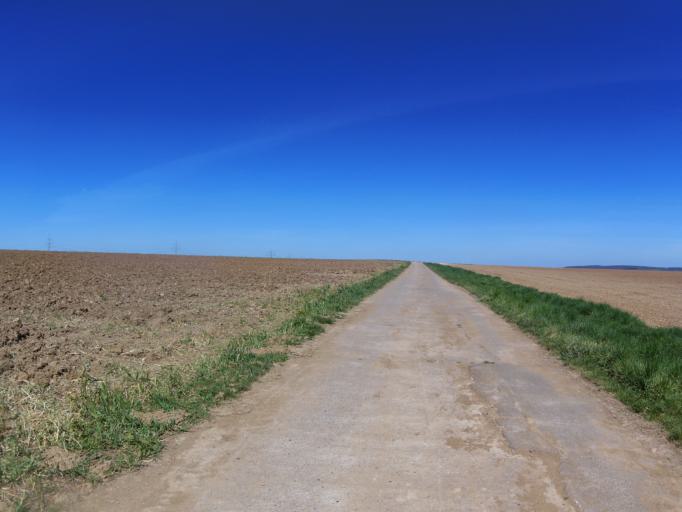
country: DE
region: Bavaria
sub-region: Regierungsbezirk Unterfranken
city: Biebelried
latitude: 49.7990
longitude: 10.0834
